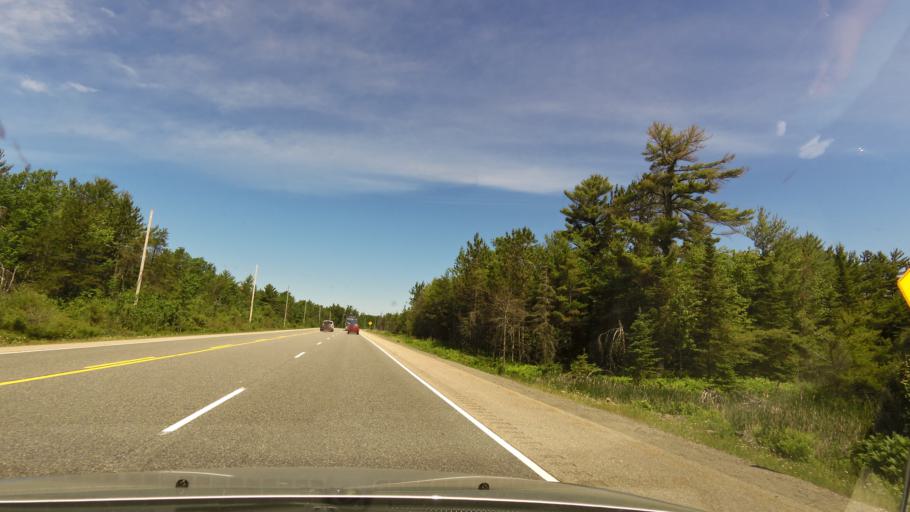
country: CA
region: Ontario
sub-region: Parry Sound District
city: Parry Sound
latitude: 45.6236
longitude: -80.3897
